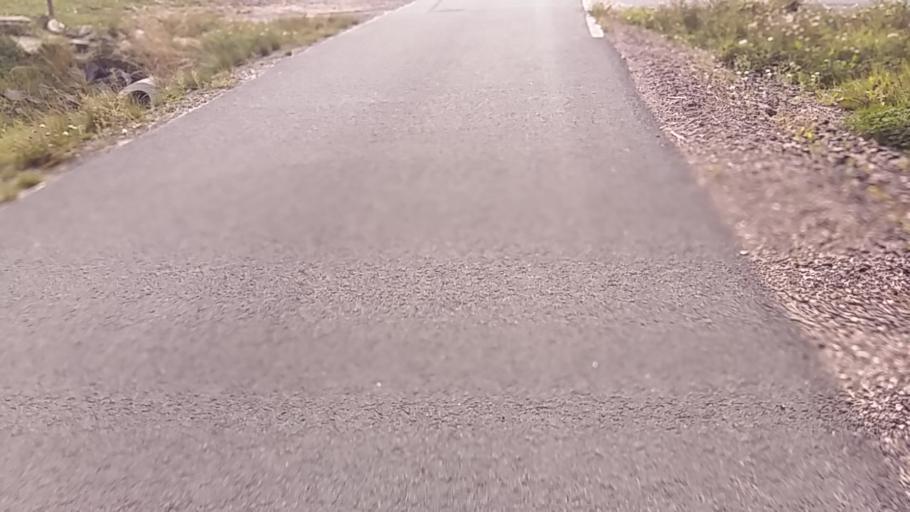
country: SE
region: Joenkoeping
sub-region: Jonkopings Kommun
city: Odensjo
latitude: 57.7289
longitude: 14.1447
